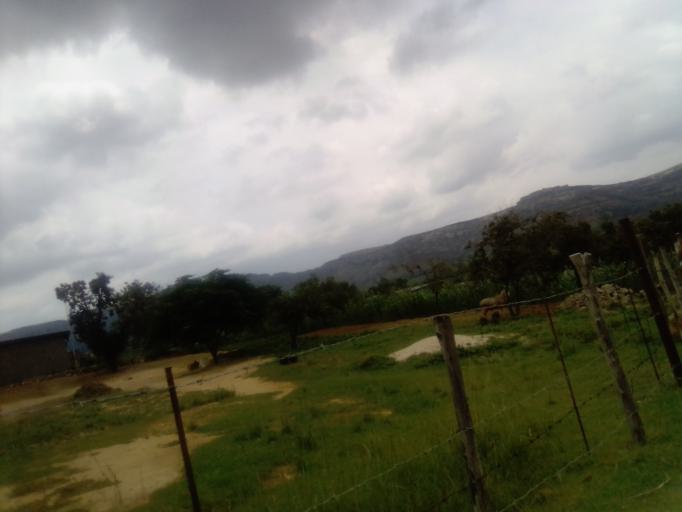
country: LS
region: Leribe
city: Leribe
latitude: -29.0293
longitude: 28.0259
